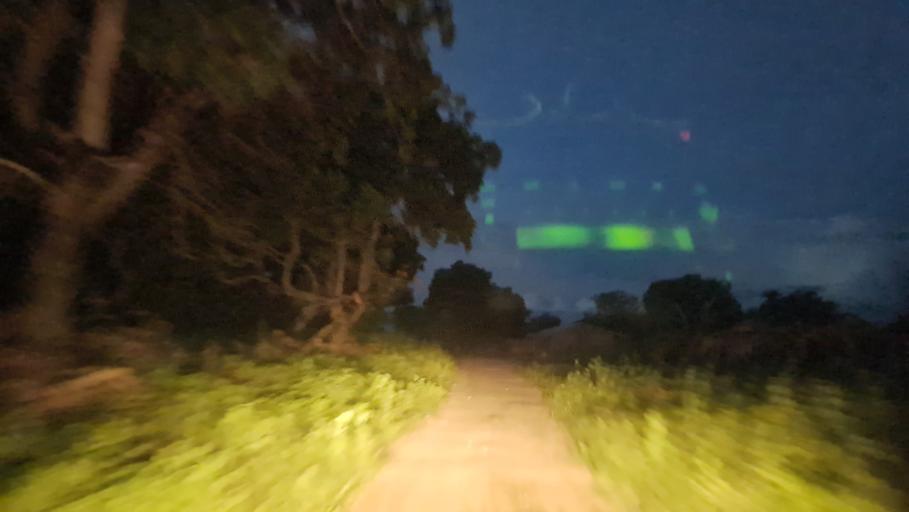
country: MZ
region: Nampula
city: Nampula
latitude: -14.6678
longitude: 39.8362
